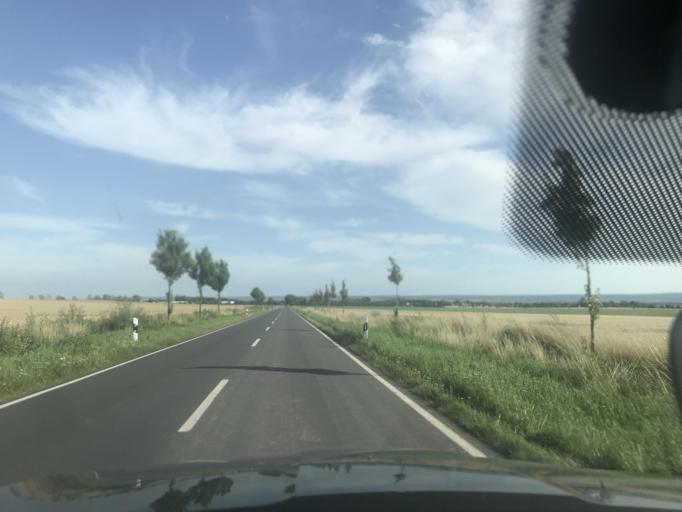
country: DE
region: Saxony-Anhalt
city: Ditfurt
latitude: 51.8483
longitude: 11.1924
